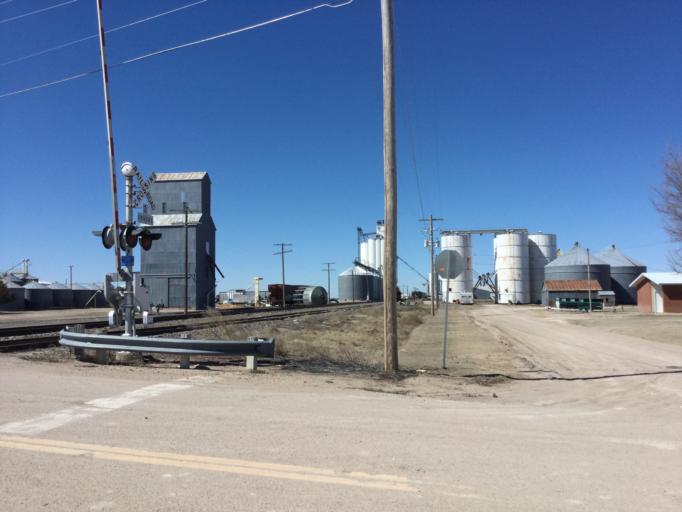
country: US
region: Kansas
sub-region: Wichita County
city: Leoti
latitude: 38.4864
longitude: -101.2131
